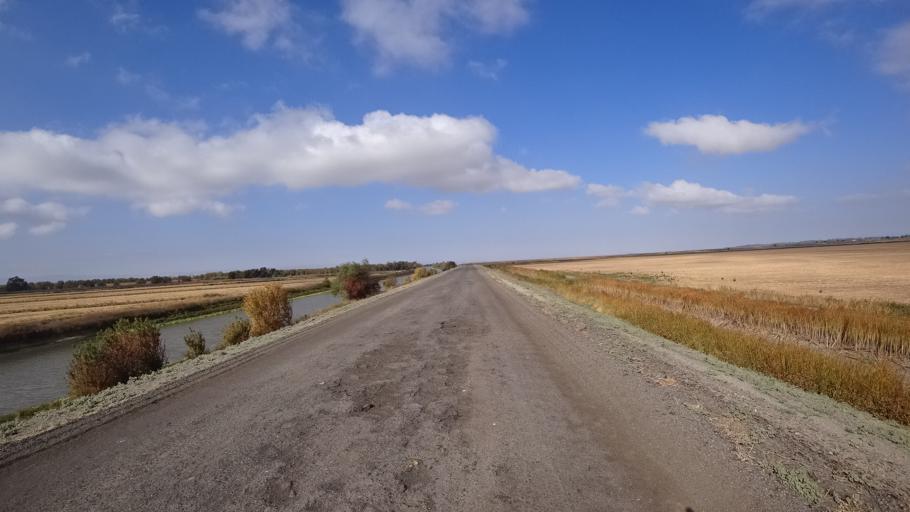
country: US
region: California
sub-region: Yolo County
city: Woodland
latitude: 38.8201
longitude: -121.7903
